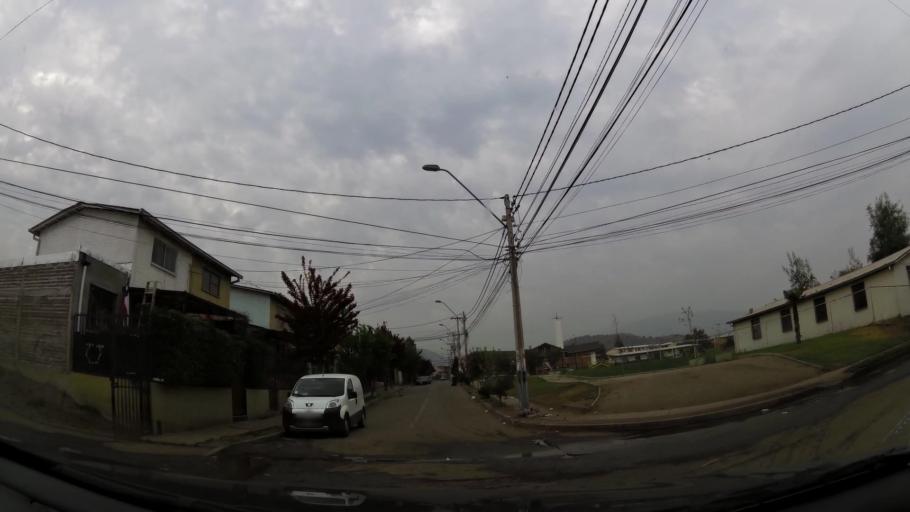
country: CL
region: Santiago Metropolitan
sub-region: Provincia de Chacabuco
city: Chicureo Abajo
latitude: -33.1903
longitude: -70.6702
